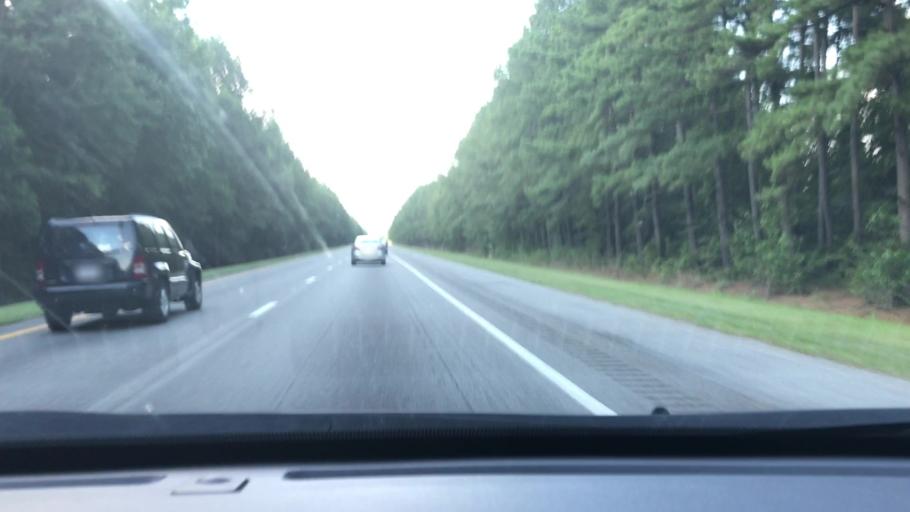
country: US
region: South Carolina
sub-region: Sumter County
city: East Sumter
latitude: 33.9165
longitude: -80.0821
